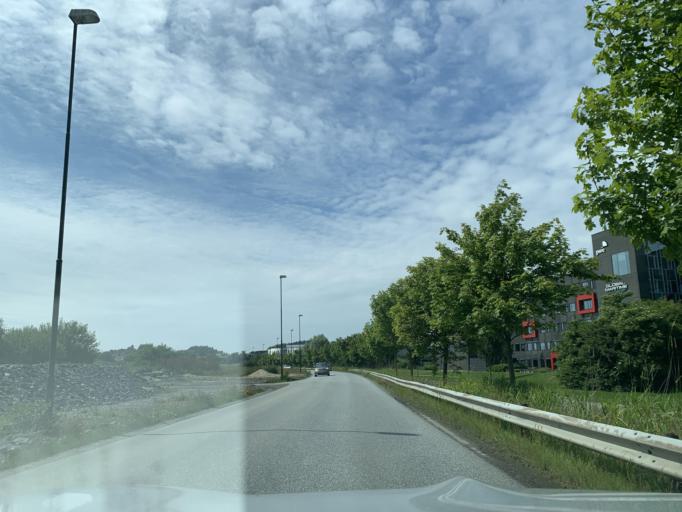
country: NO
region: Rogaland
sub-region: Sola
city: Sola
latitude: 58.8944
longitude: 5.6888
